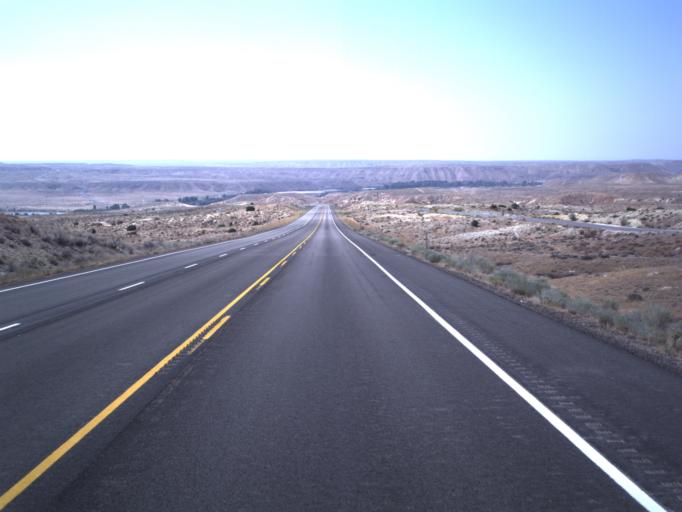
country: US
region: Utah
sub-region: Uintah County
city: Naples
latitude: 40.3363
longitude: -109.4850
